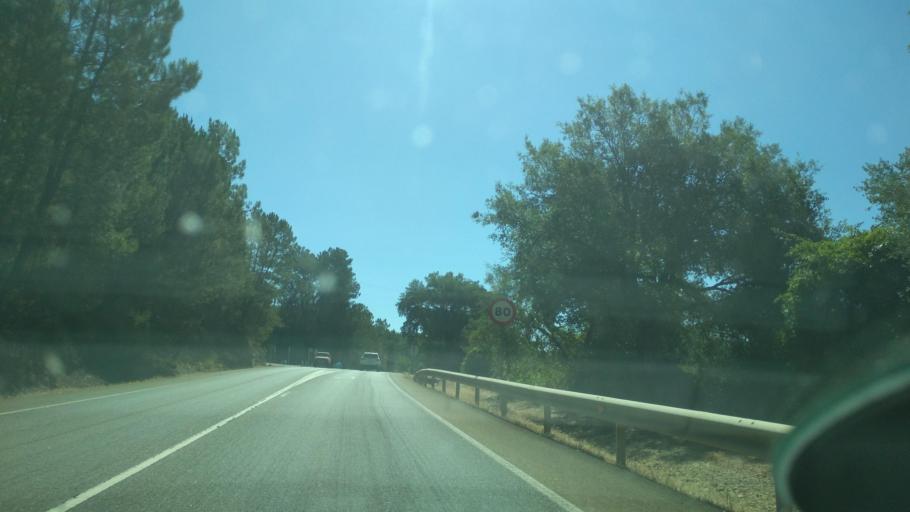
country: ES
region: Andalusia
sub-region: Provincia de Huelva
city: Fuenteheridos
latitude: 37.9165
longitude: -6.6684
